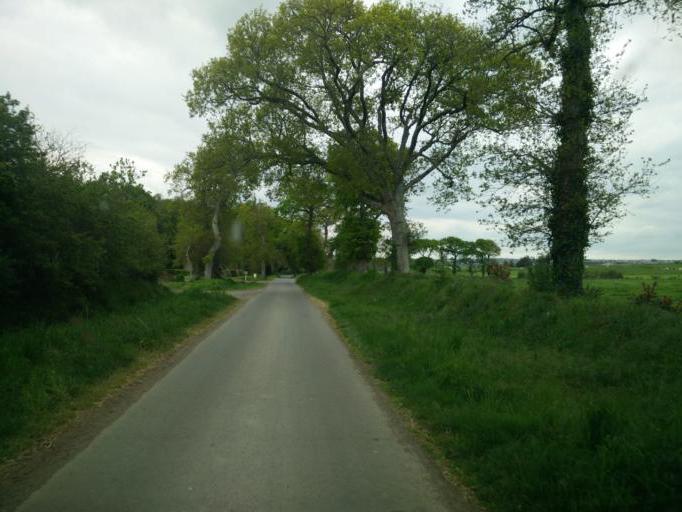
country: FR
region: Brittany
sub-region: Departement des Cotes-d'Armor
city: Hillion
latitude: 48.5079
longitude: -2.6721
